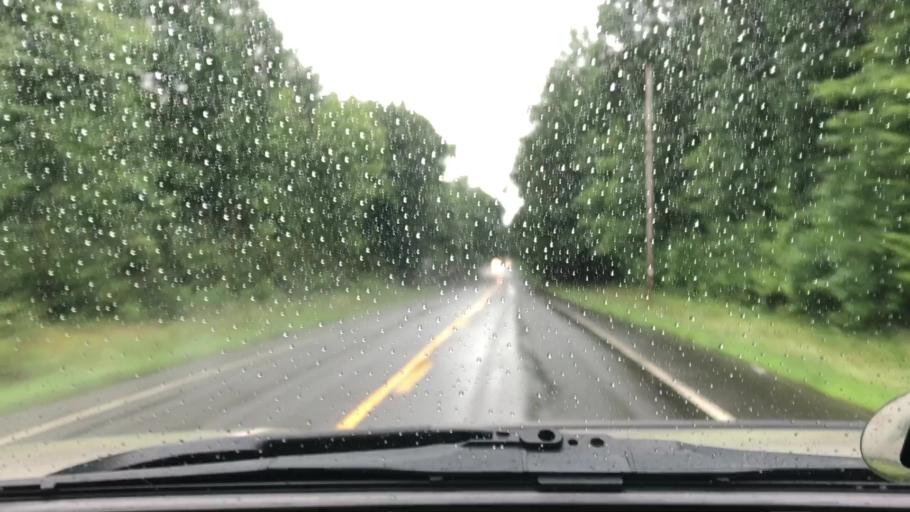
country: US
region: New York
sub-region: Greene County
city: Palenville
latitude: 42.1700
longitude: -73.9892
